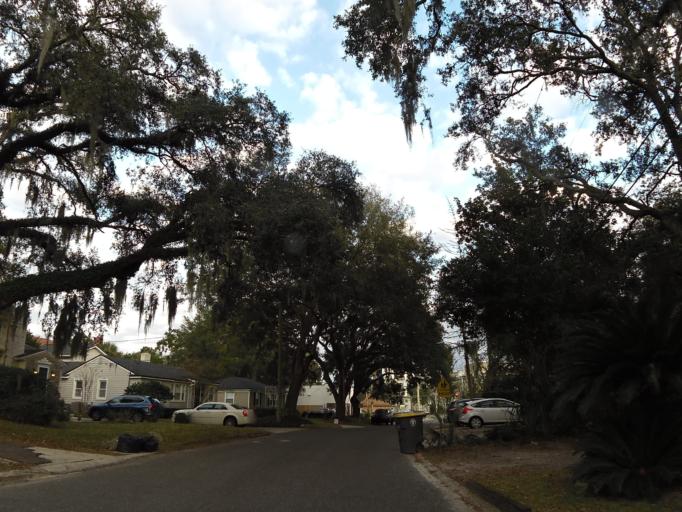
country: US
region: Florida
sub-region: Duval County
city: Jacksonville
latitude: 30.2911
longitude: -81.7150
